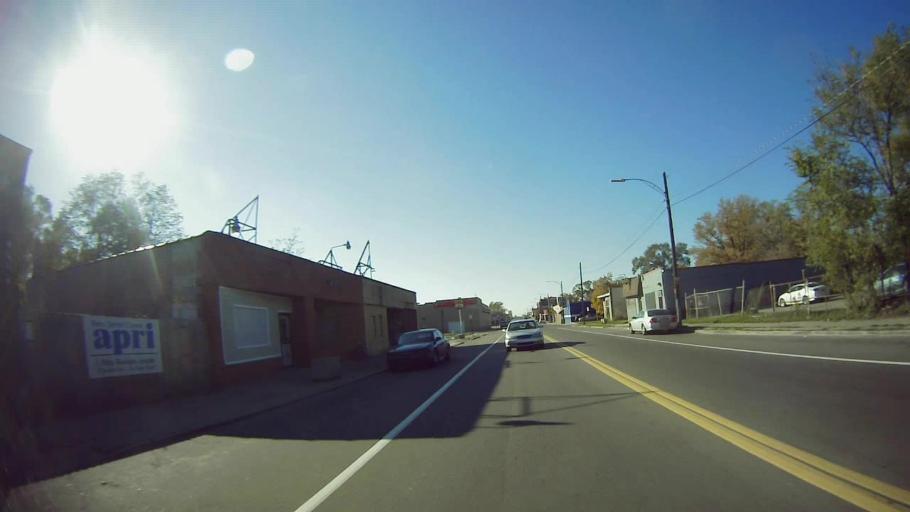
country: US
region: Michigan
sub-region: Wayne County
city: Highland Park
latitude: 42.4332
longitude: -83.0807
